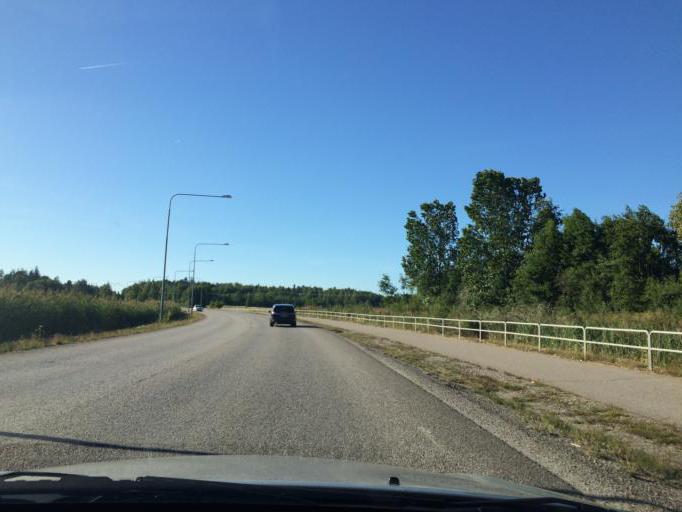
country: SE
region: Soedermanland
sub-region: Eskilstuna Kommun
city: Torshalla
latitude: 59.3934
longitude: 16.4510
